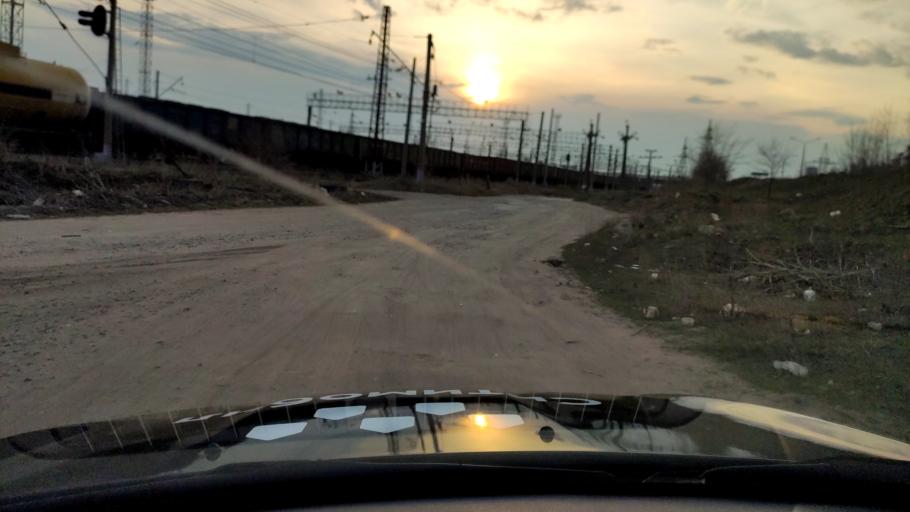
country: RU
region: Samara
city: Zhigulevsk
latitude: 53.4795
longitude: 49.5242
